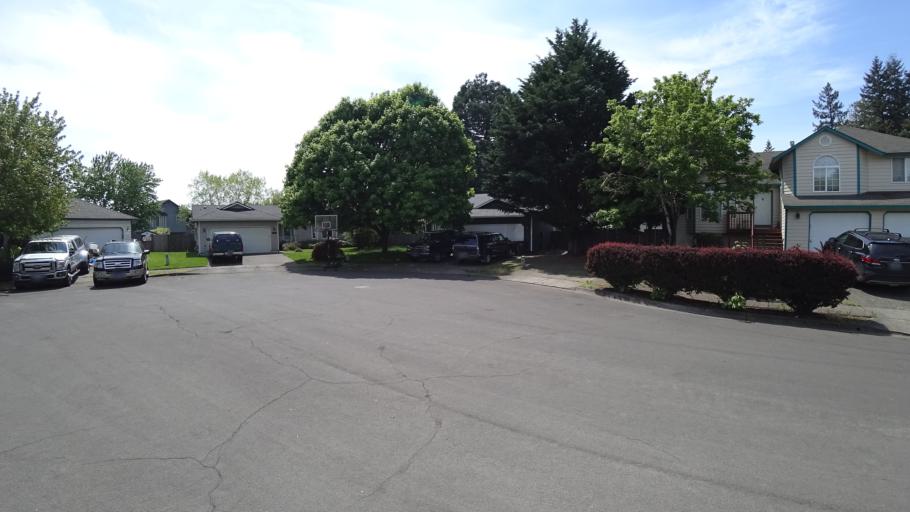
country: US
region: Oregon
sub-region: Washington County
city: Hillsboro
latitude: 45.5057
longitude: -122.9305
